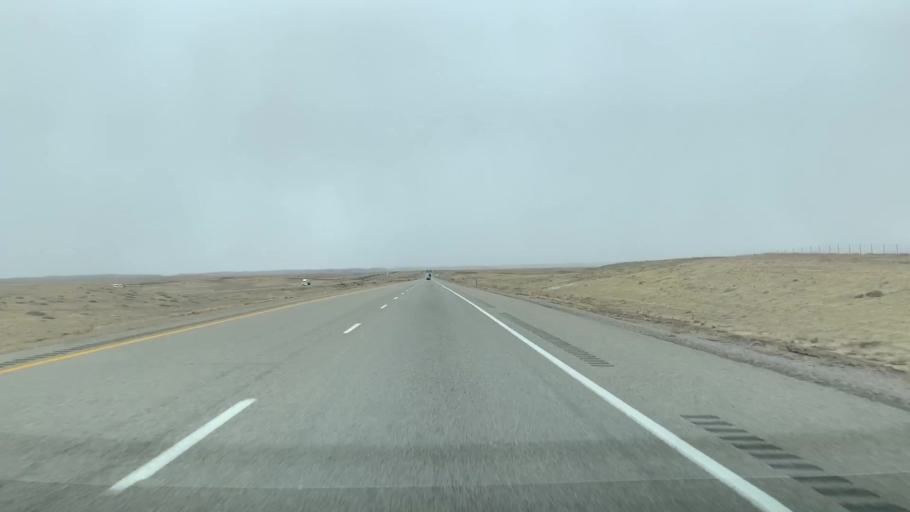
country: US
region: Utah
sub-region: Carbon County
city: East Carbon City
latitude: 38.9656
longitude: -110.2779
